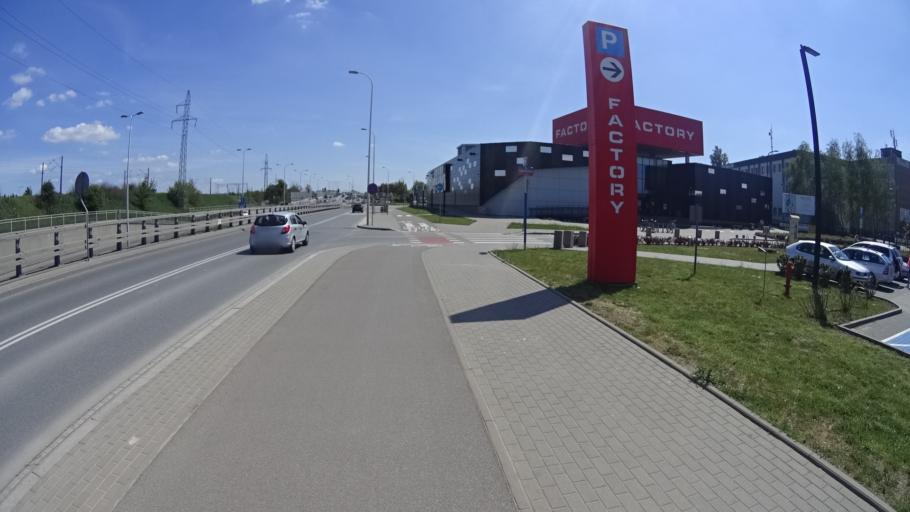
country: PL
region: Masovian Voivodeship
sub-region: Warszawa
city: Ursus
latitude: 52.2035
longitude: 20.8934
